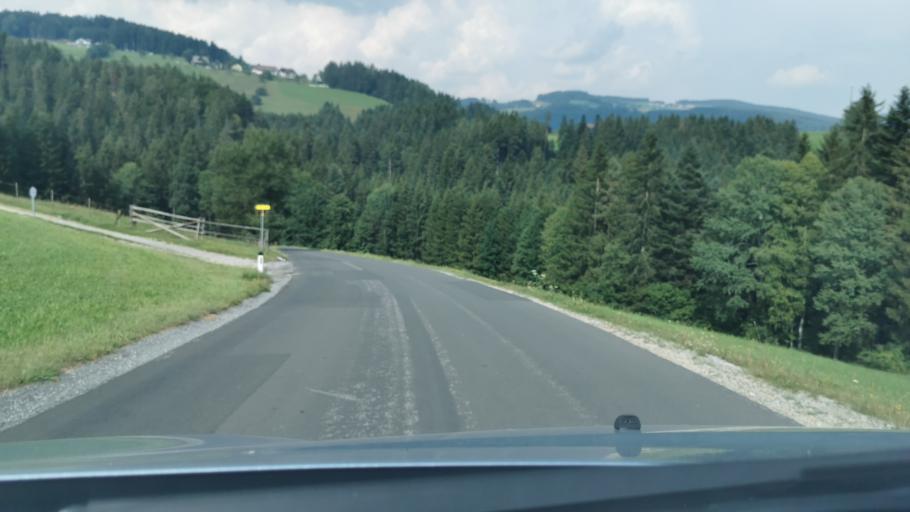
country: AT
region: Styria
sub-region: Politischer Bezirk Weiz
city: Strallegg
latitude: 47.3977
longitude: 15.6857
